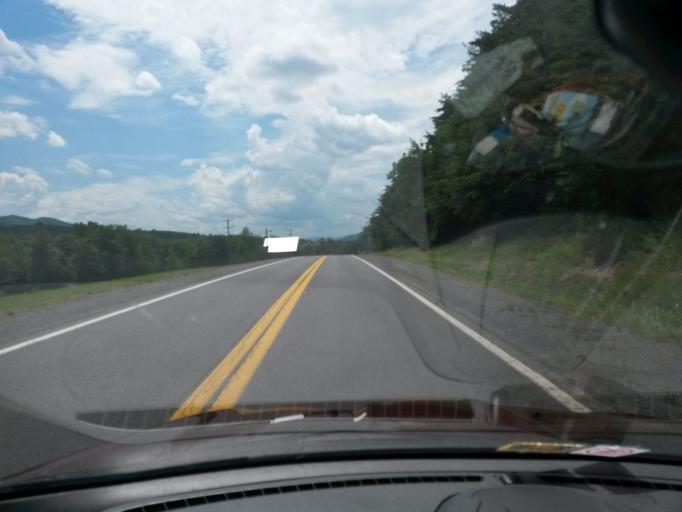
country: US
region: West Virginia
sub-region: Grant County
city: Petersburg
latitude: 38.9294
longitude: -79.1733
